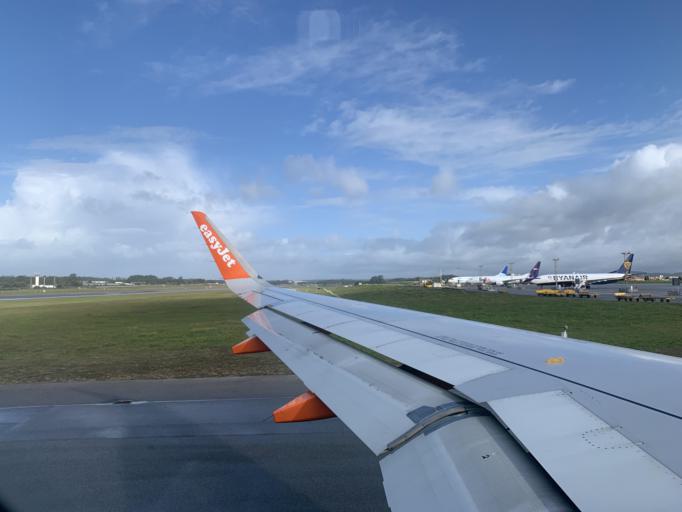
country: PT
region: Porto
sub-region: Matosinhos
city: Santa Cruz do Bispo
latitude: 41.2391
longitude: -8.6772
